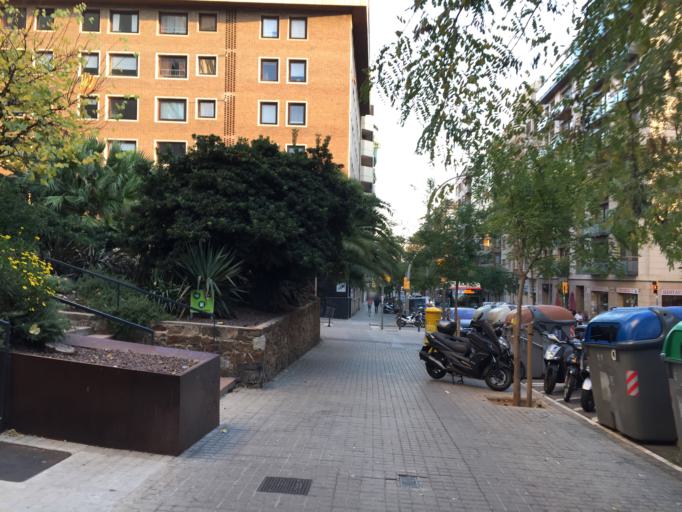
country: ES
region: Catalonia
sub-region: Provincia de Barcelona
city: Gracia
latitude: 41.4075
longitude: 2.1611
